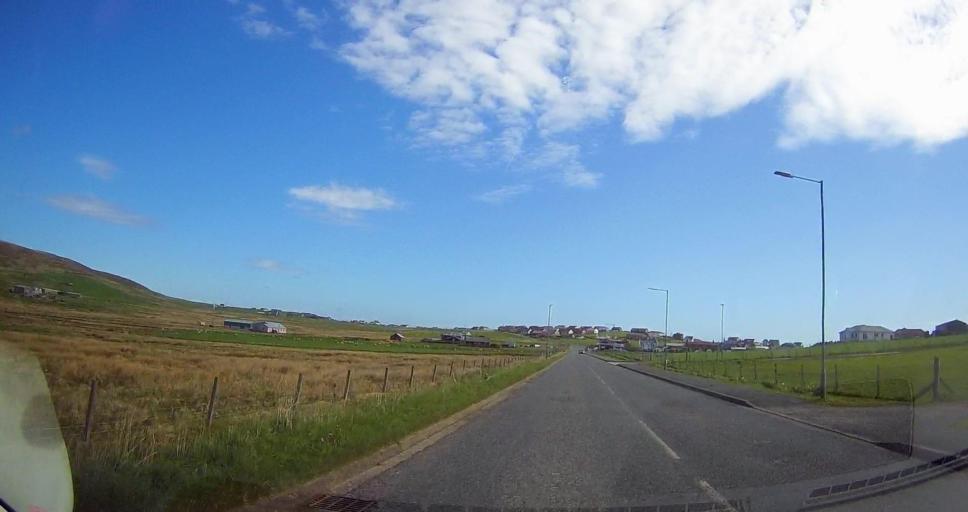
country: GB
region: Scotland
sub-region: Shetland Islands
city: Sandwick
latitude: 60.0005
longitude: -1.2415
